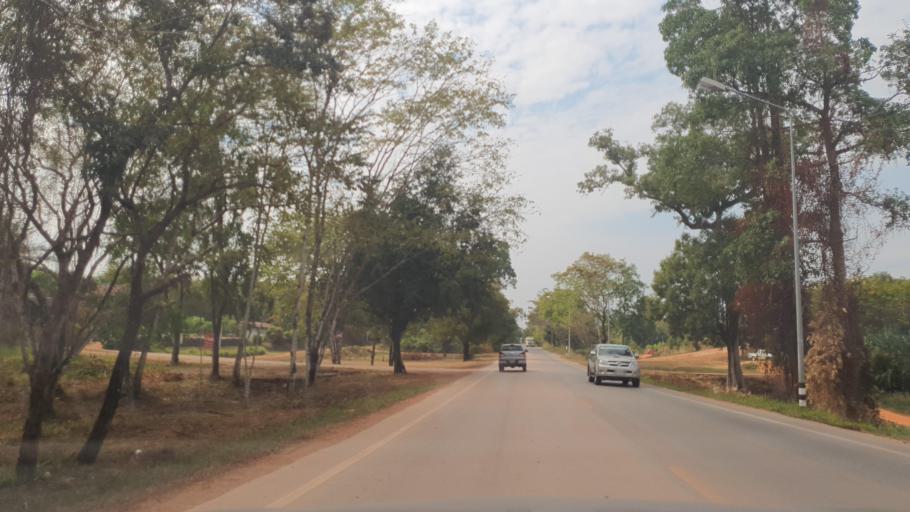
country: TH
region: Changwat Bueng Kan
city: Bung Khla
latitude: 18.2808
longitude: 103.8738
